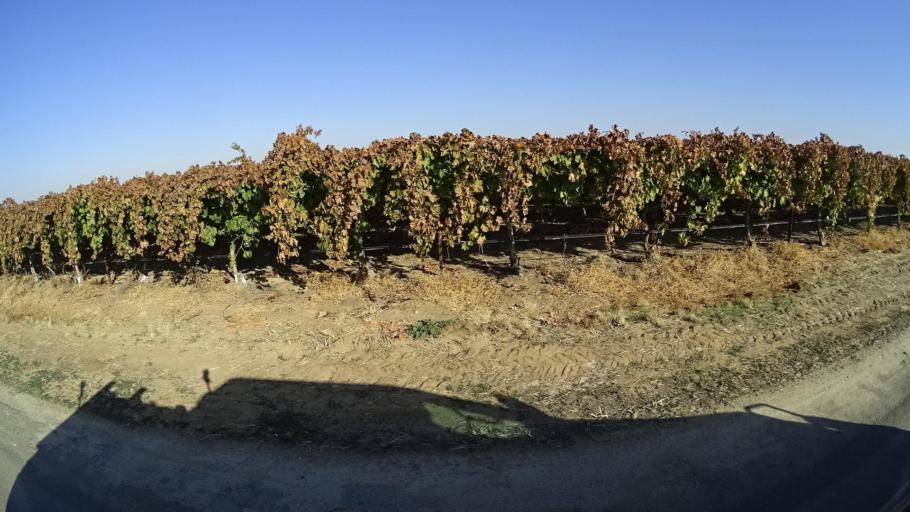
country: US
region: California
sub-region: Kern County
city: McFarland
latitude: 35.7253
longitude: -119.1659
